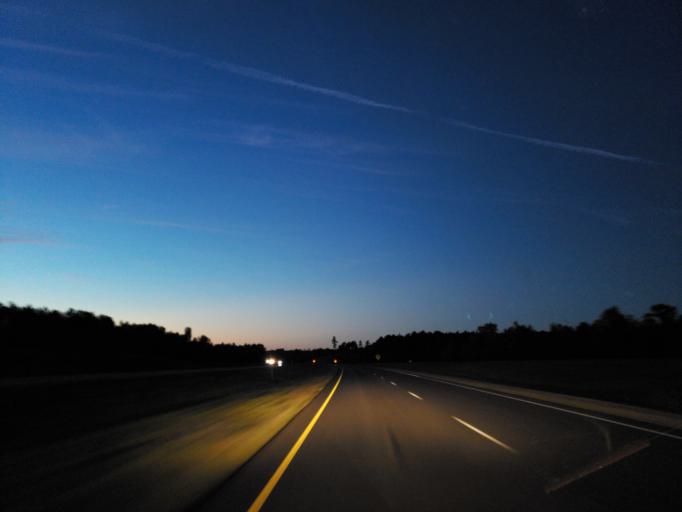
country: US
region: Mississippi
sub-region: Clarke County
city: Quitman
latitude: 32.0606
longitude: -88.6787
